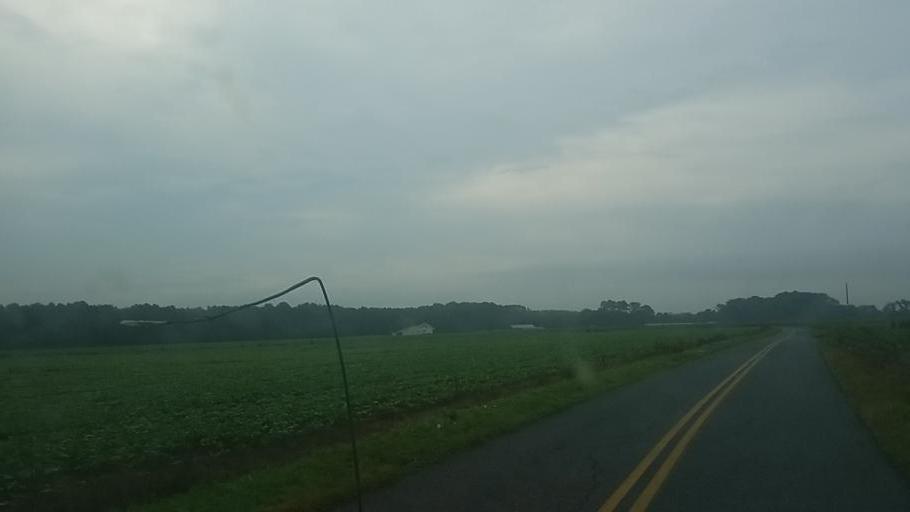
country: US
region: Maryland
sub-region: Wicomico County
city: Pittsville
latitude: 38.4240
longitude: -75.3192
